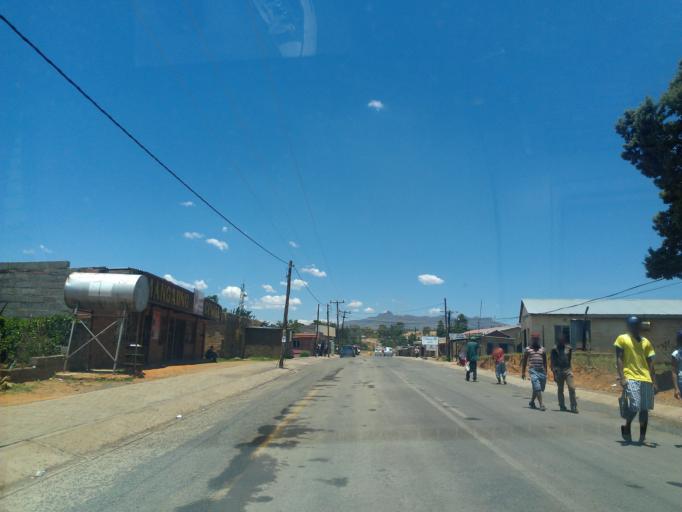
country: LS
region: Berea
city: Teyateyaneng
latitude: -29.1099
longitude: 27.9657
